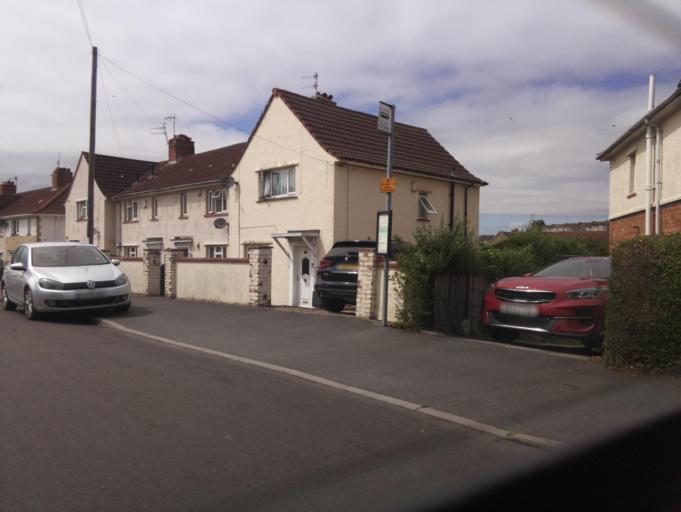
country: GB
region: England
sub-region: Bristol
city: Bristol
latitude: 51.4336
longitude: -2.5920
